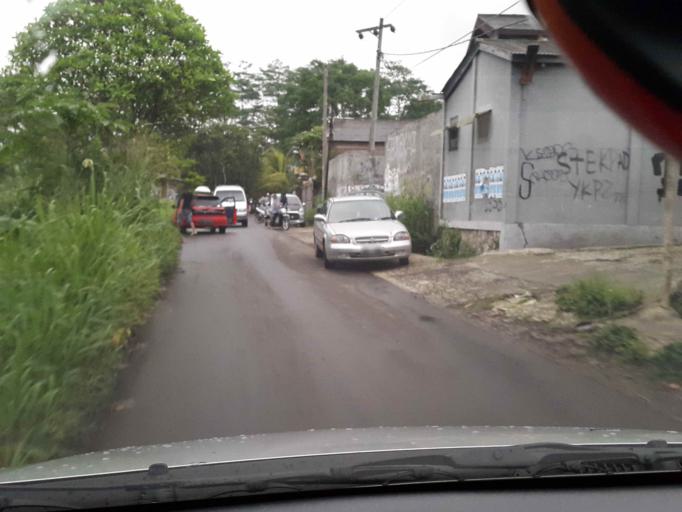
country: ID
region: West Java
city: Sukabumi
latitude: -6.9141
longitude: 106.8735
